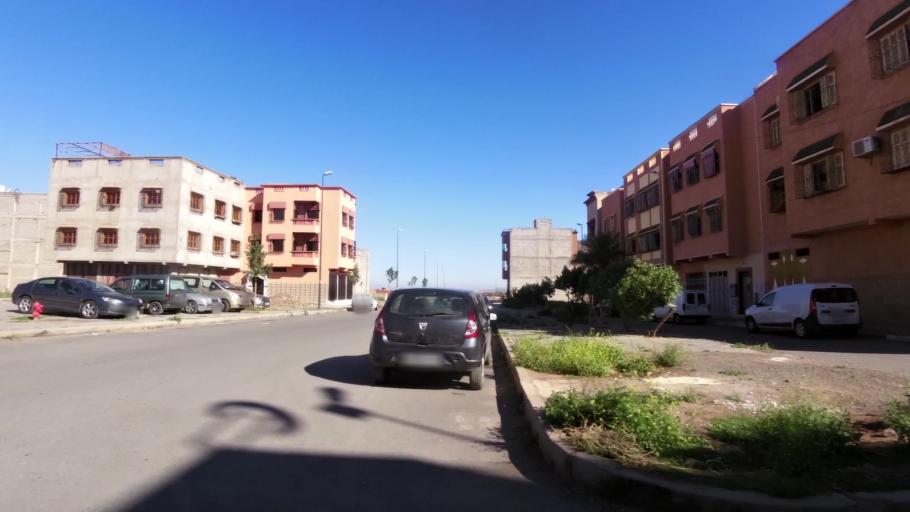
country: MA
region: Marrakech-Tensift-Al Haouz
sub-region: Marrakech
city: Marrakesh
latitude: 31.6013
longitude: -8.0381
